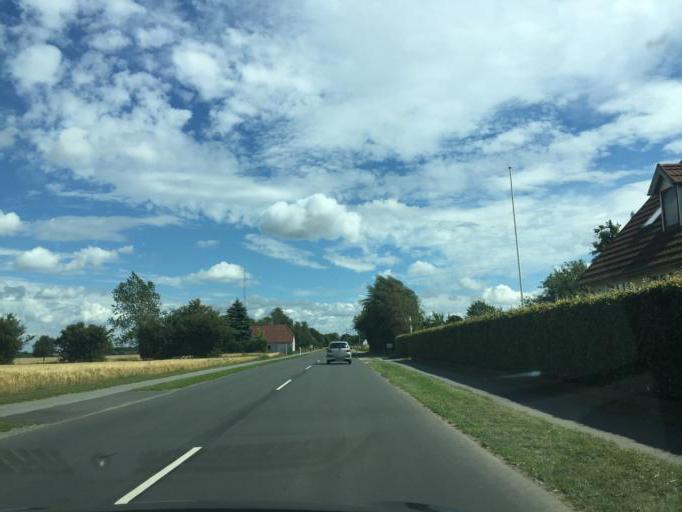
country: DK
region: South Denmark
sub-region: Nordfyns Kommune
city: Otterup
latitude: 55.5210
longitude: 10.3683
